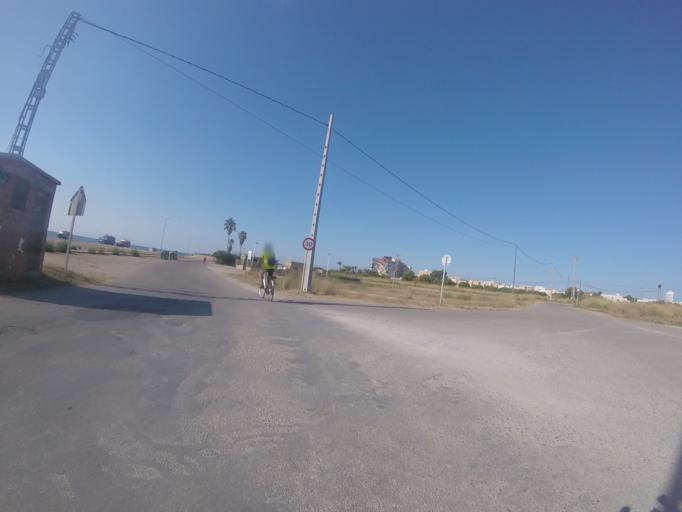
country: ES
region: Valencia
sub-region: Provincia de Castello
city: Benicarlo
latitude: 40.4189
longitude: 0.4361
